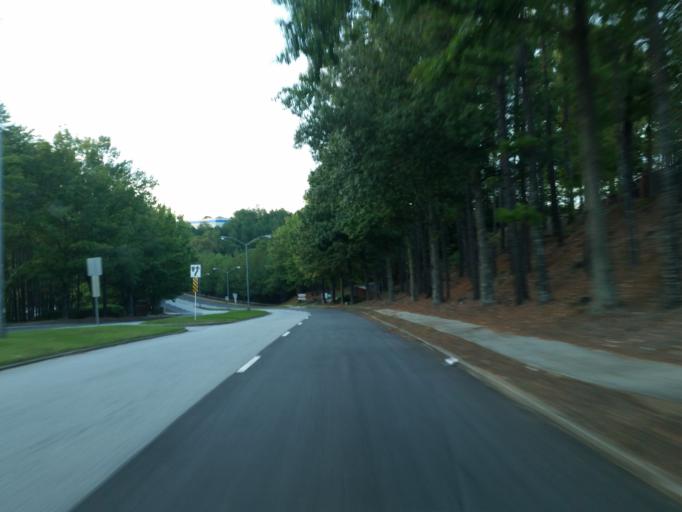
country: US
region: Georgia
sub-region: Cobb County
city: Smyrna
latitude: 33.8334
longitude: -84.5165
